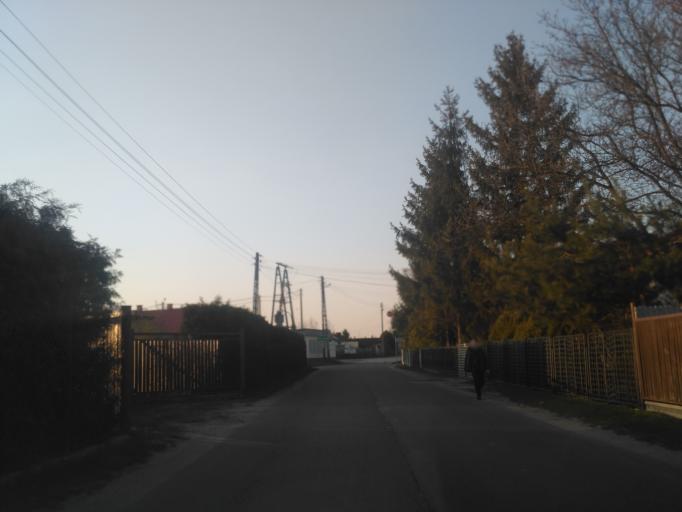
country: PL
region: Lublin Voivodeship
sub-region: Powiat chelmski
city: Pokrowka
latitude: 51.1125
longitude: 23.4835
